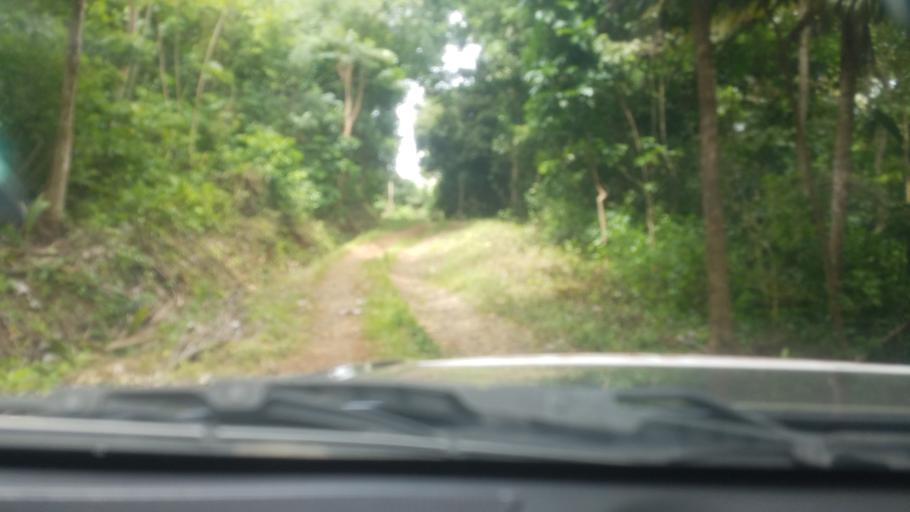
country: LC
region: Micoud Quarter
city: Micoud
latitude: 13.8062
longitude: -60.9370
